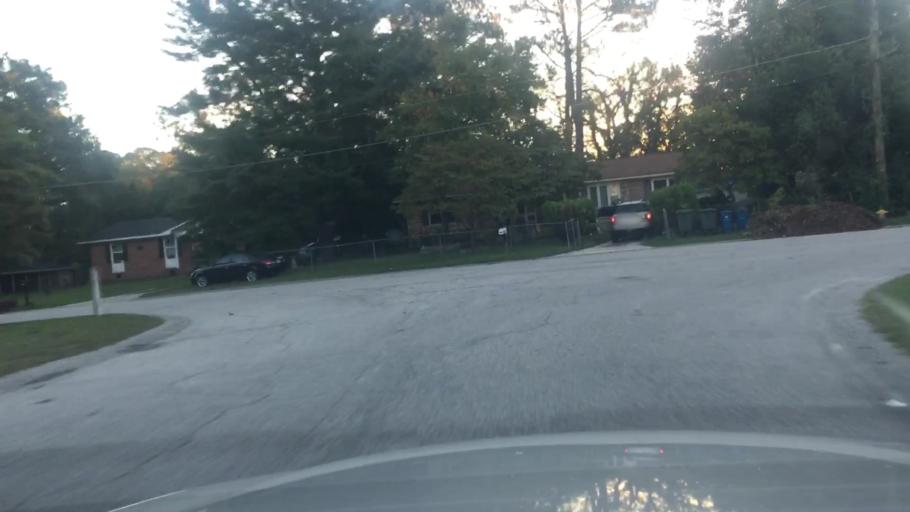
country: US
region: North Carolina
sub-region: Cumberland County
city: Hope Mills
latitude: 35.0185
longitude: -78.9649
